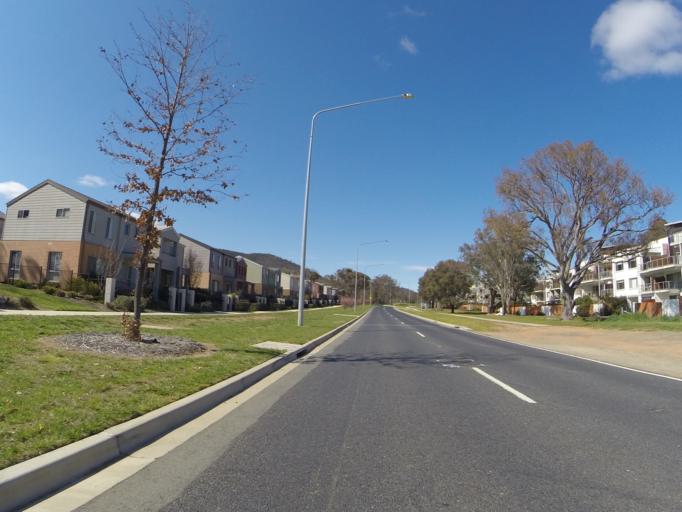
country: AU
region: Australian Capital Territory
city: Kaleen
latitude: -35.2264
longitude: 149.1660
